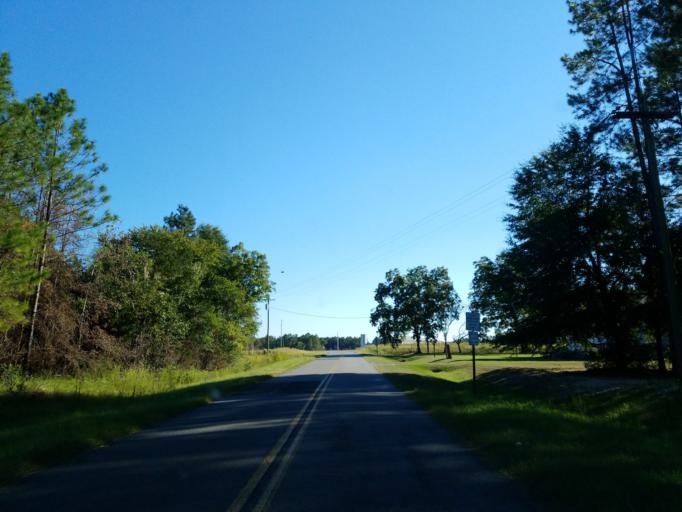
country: US
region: Georgia
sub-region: Dooly County
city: Vienna
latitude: 32.0729
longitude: -83.9559
